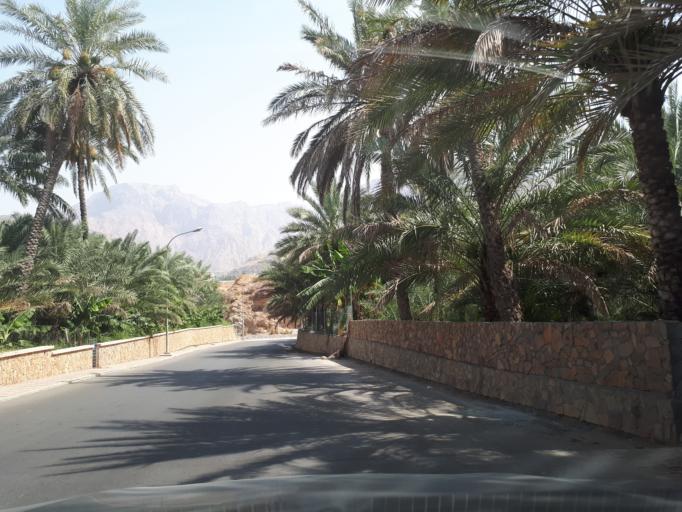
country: OM
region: Ash Sharqiyah
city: Ibra'
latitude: 23.0906
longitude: 58.8630
